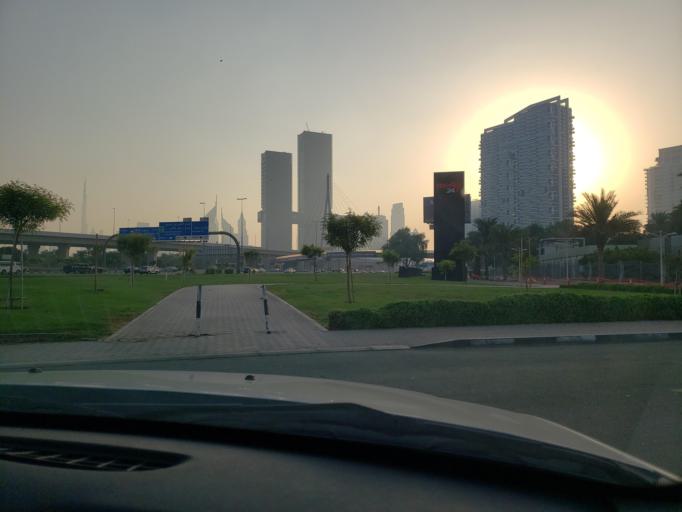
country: AE
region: Ash Shariqah
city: Sharjah
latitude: 25.2331
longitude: 55.3011
